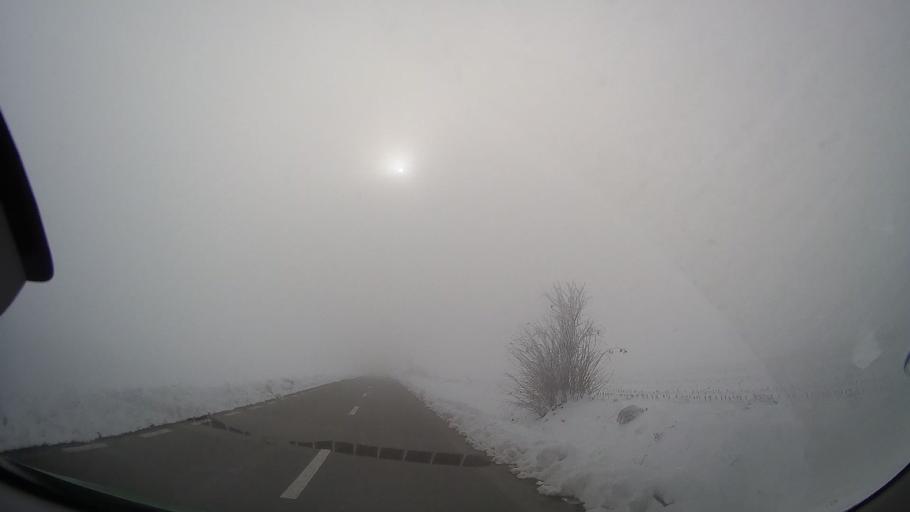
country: RO
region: Iasi
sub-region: Comuna Valea Seaca
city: Valea Seaca
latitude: 47.2789
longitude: 26.6706
